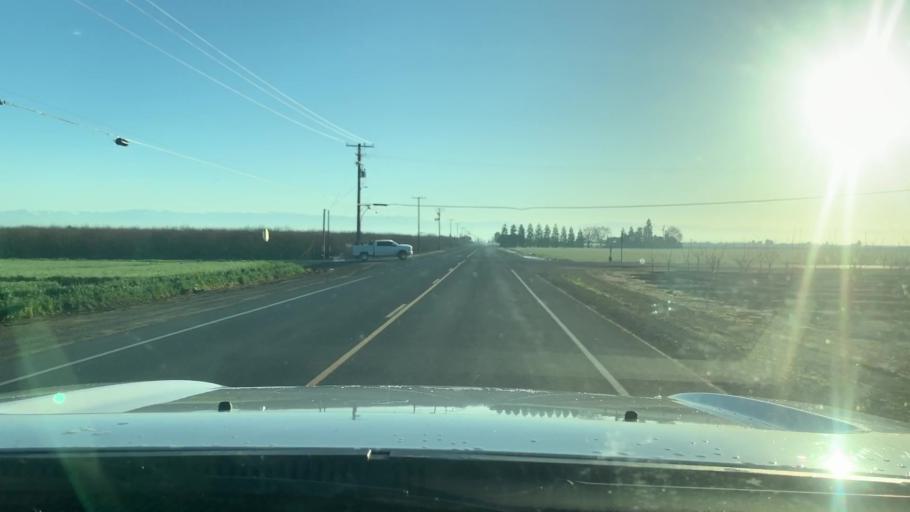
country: US
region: California
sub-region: Kings County
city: Corcoran
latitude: 36.2108
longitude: -119.4938
